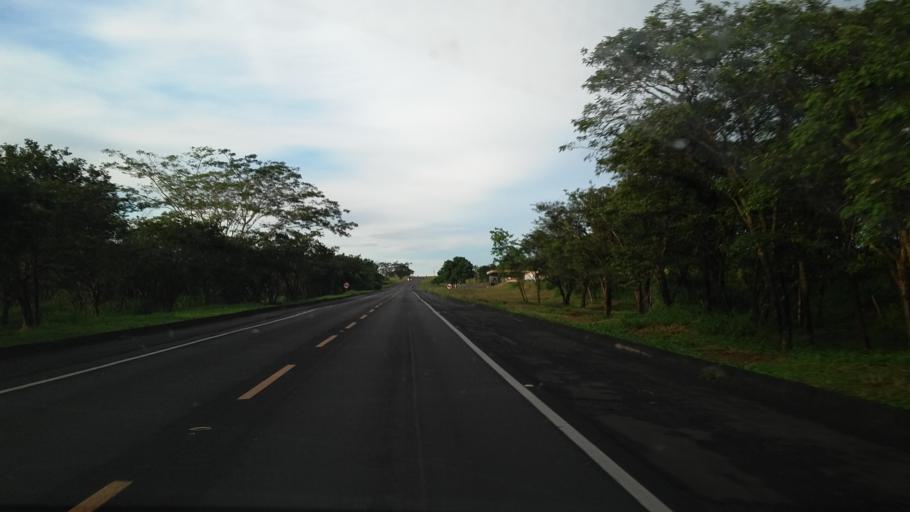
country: BR
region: Sao Paulo
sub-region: Marilia
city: Marilia
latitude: -21.9231
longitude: -49.9170
